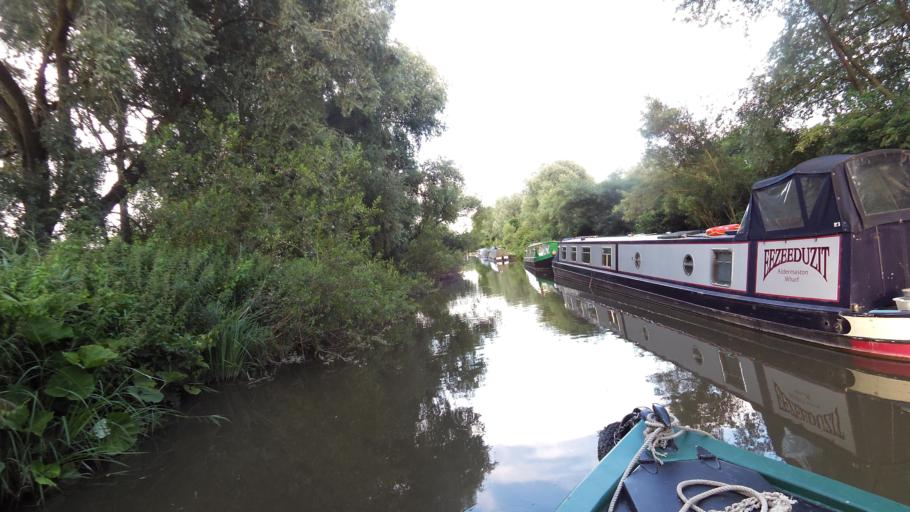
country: GB
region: England
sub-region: Hampshire
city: Tadley
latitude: 51.3959
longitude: -1.1831
